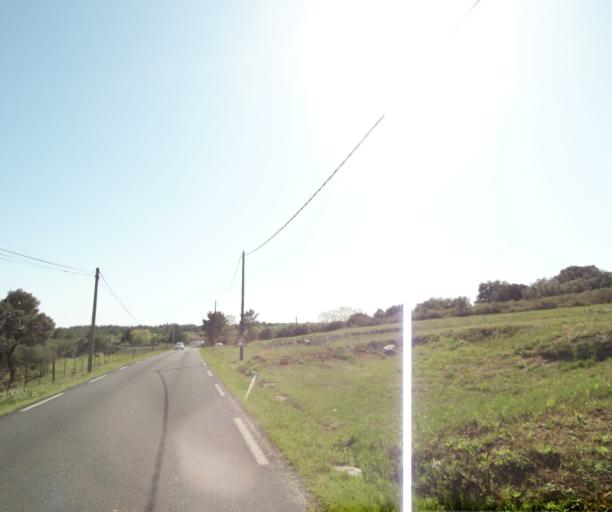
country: FR
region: Languedoc-Roussillon
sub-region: Departement de l'Herault
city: Castries
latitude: 43.6965
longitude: 3.9608
